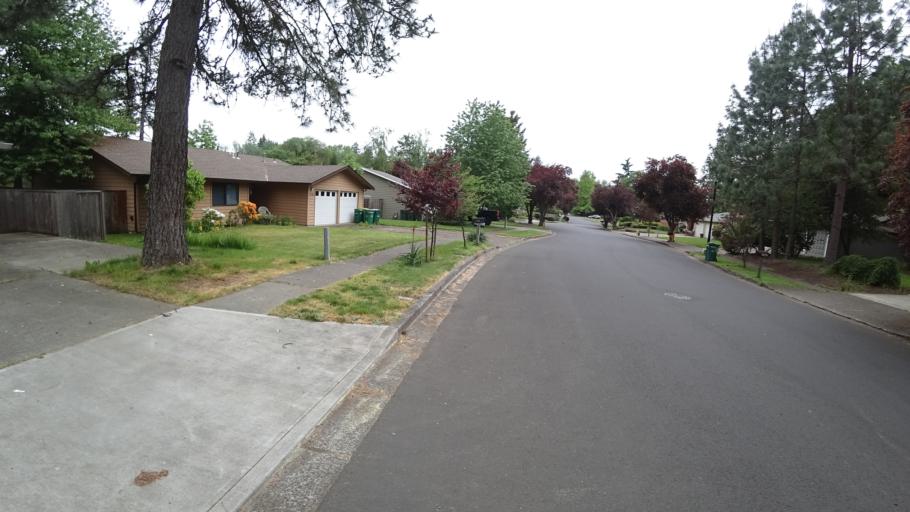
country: US
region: Oregon
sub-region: Washington County
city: Raleigh Hills
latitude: 45.4689
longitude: -122.7822
